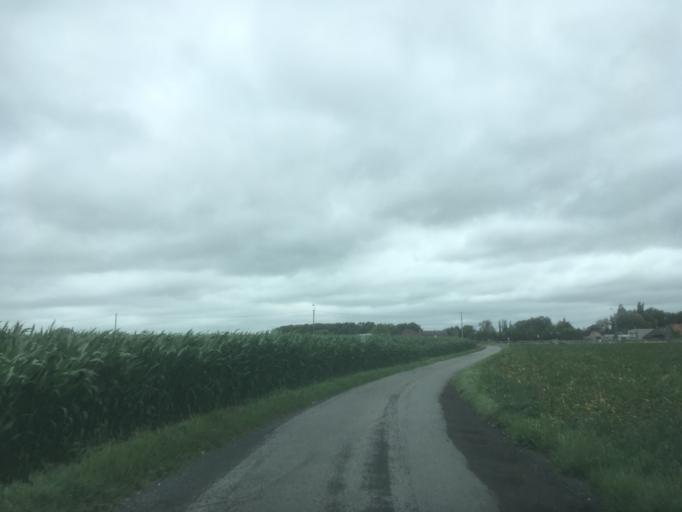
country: BE
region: Flanders
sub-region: Provincie West-Vlaanderen
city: Moorslede
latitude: 50.9317
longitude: 3.0763
